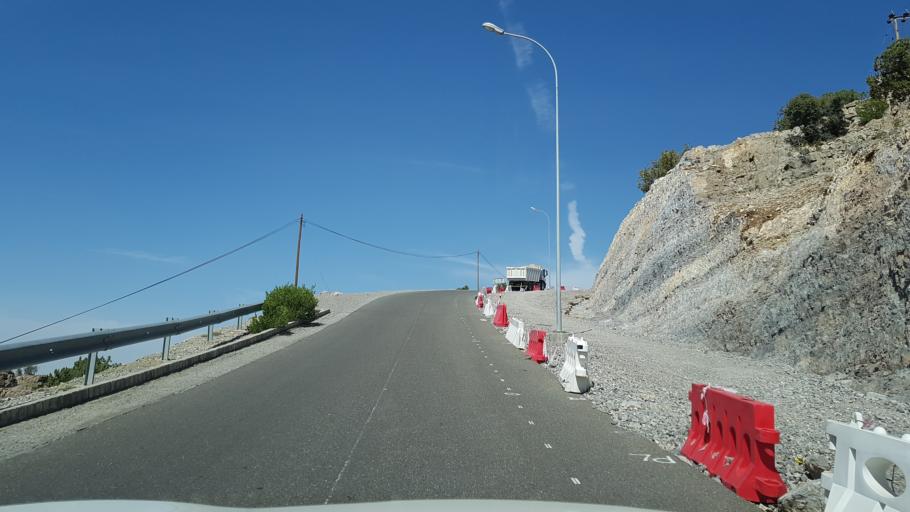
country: OM
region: Muhafazat ad Dakhiliyah
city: Izki
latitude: 23.1135
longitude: 57.6505
